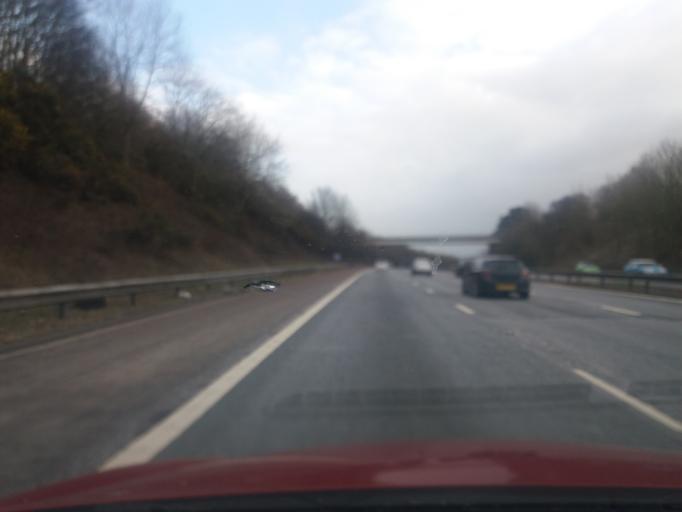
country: GB
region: England
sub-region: Lancashire
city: Clayton-le-Woods
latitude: 53.6962
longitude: -2.6281
